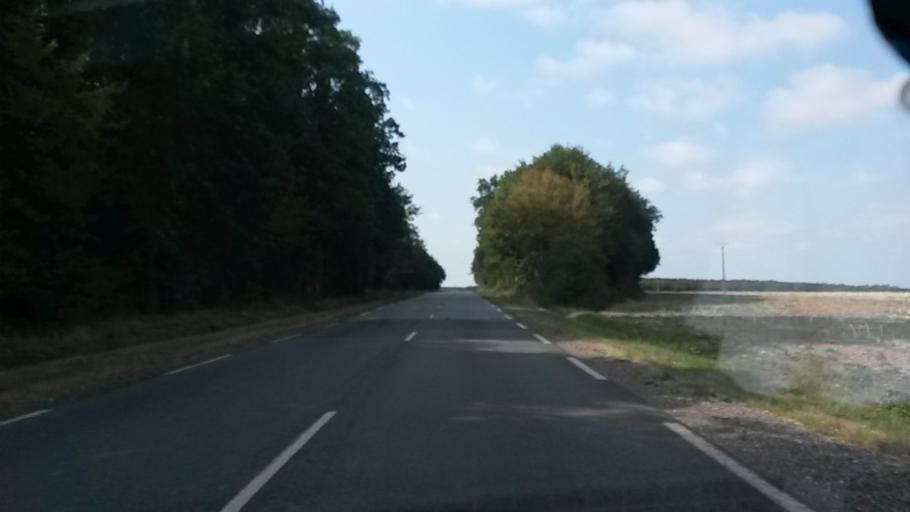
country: FR
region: Haute-Normandie
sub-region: Departement de l'Eure
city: Damville
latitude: 48.8557
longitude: 1.0623
